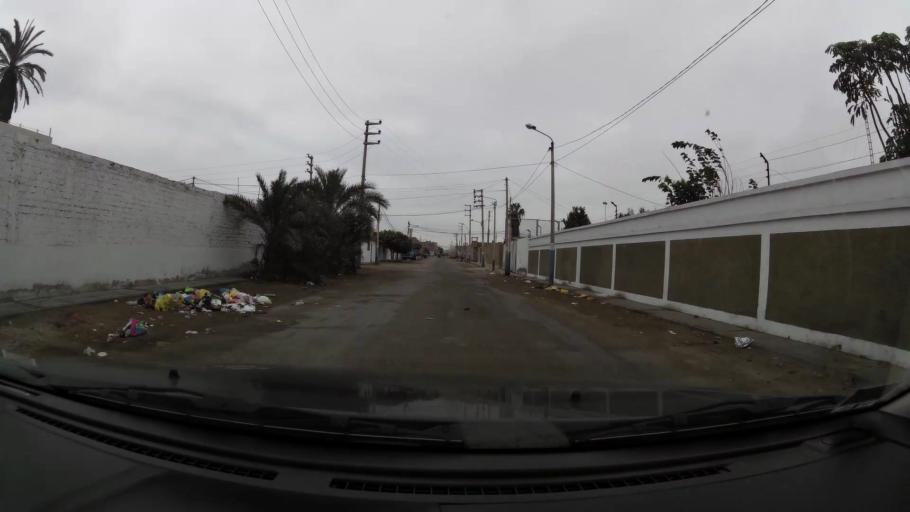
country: PE
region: Ica
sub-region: Provincia de Pisco
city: Pisco
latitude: -13.7368
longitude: -76.2254
